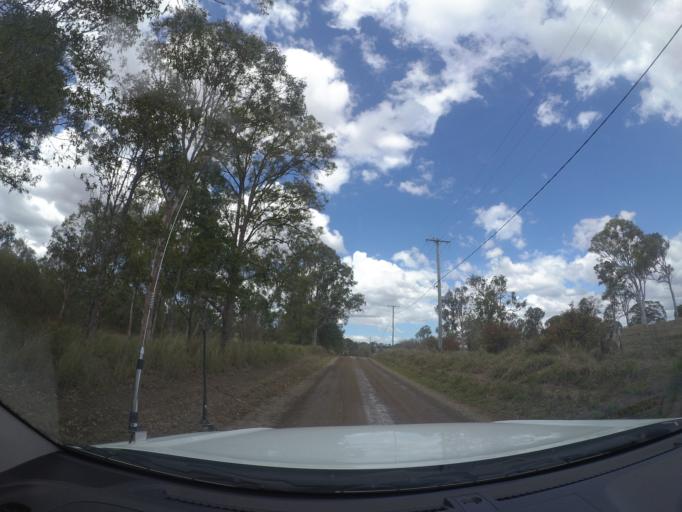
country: AU
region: Queensland
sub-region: Logan
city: Cedar Vale
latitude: -27.9060
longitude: 152.9730
